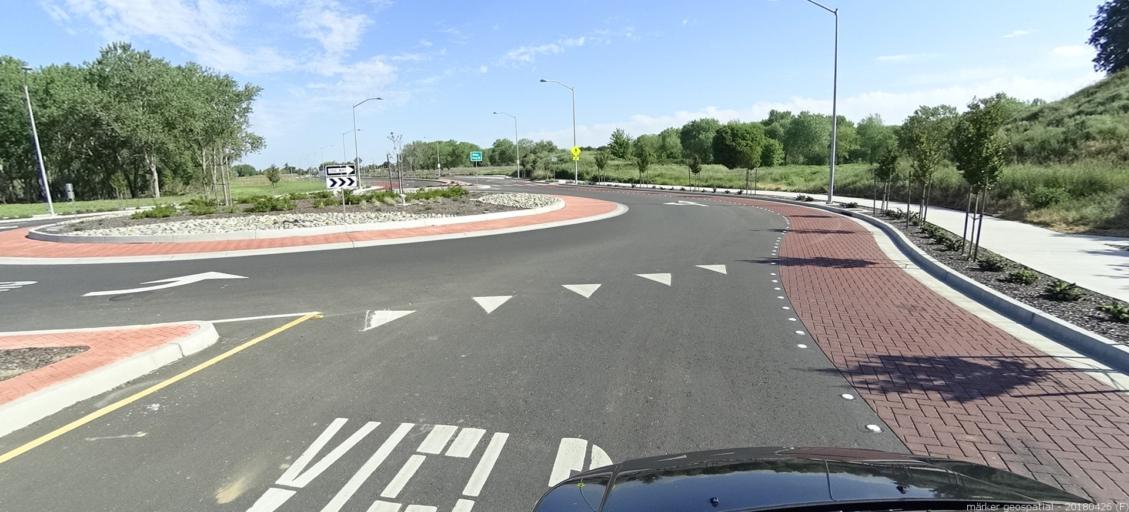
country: US
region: California
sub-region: Yolo County
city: West Sacramento
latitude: 38.5545
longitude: -121.5216
